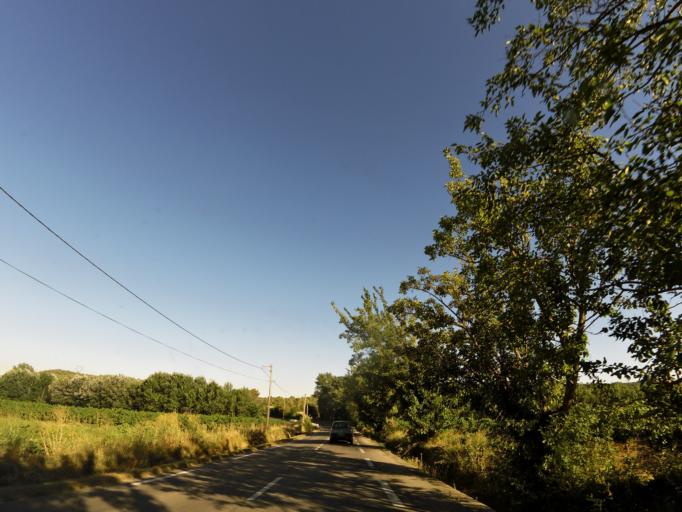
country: FR
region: Languedoc-Roussillon
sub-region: Departement du Gard
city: Sommieres
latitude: 43.8291
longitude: 4.0432
